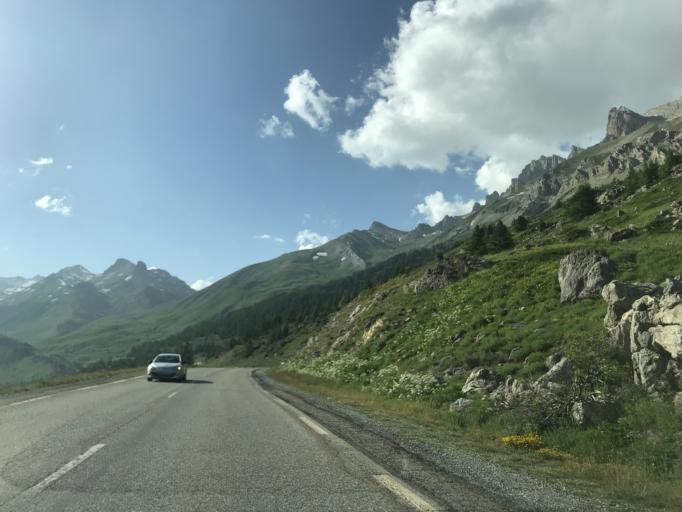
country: FR
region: Provence-Alpes-Cote d'Azur
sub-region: Departement des Hautes-Alpes
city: Le Monetier-les-Bains
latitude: 45.0333
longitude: 6.4392
